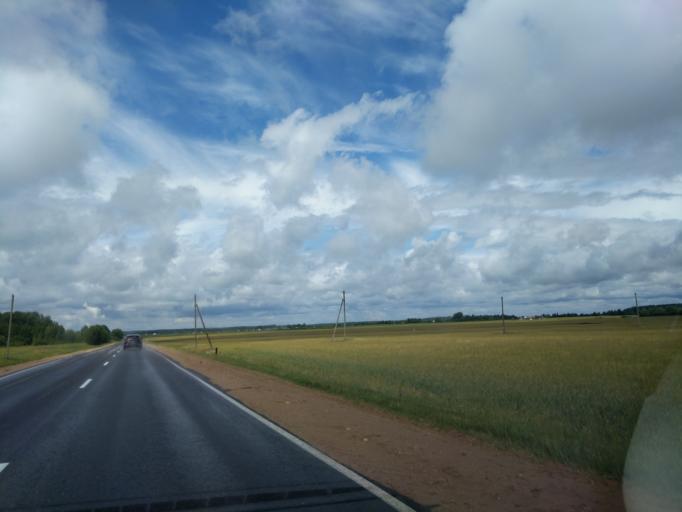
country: BY
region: Minsk
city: Il'ya
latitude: 54.3836
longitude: 27.3657
